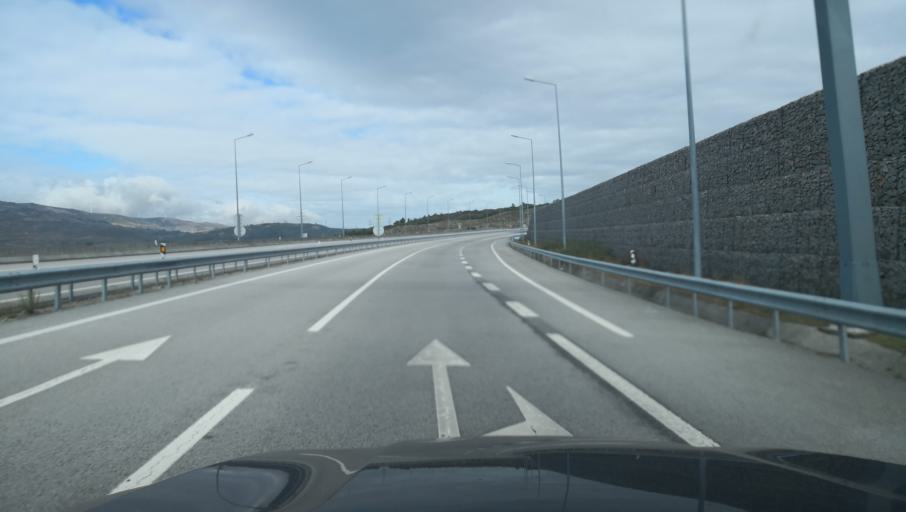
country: PT
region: Vila Real
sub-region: Vila Real
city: Vila Real
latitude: 41.3560
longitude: -7.7021
